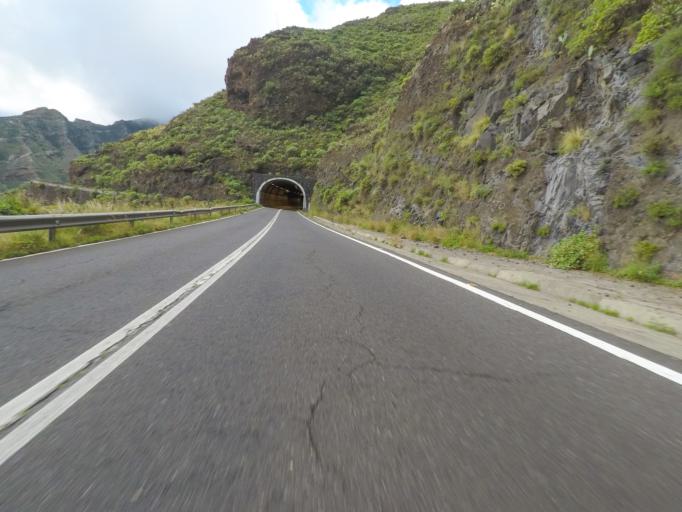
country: ES
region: Canary Islands
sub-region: Provincia de Santa Cruz de Tenerife
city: Hermigua
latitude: 28.1287
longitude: -17.1729
